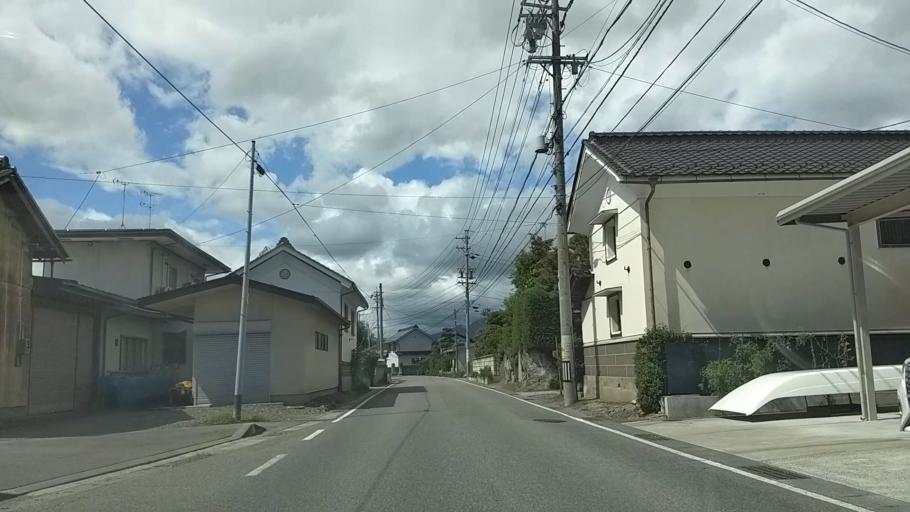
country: JP
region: Nagano
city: Nagano-shi
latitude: 36.6092
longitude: 138.2082
